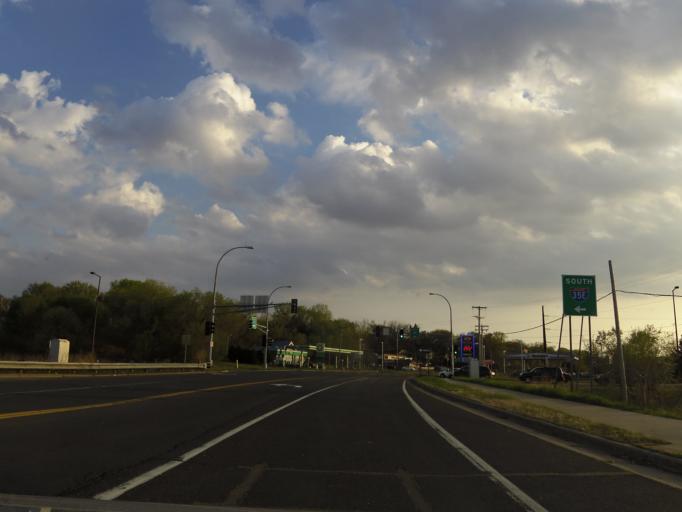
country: US
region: Minnesota
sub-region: Dakota County
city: Mendota Heights
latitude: 44.9010
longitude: -93.1364
